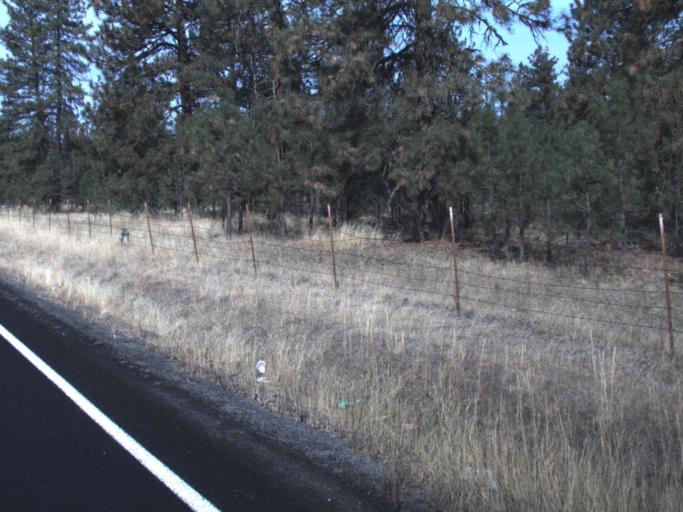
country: US
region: Washington
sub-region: Spokane County
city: Fairchild Air Force Base
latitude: 47.8393
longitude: -117.7972
